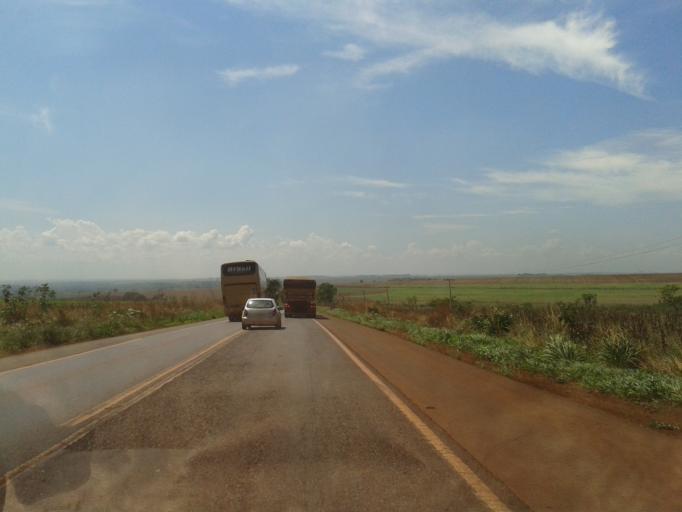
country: BR
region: Goias
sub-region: Santa Helena De Goias
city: Santa Helena de Goias
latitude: -18.0229
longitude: -50.3312
